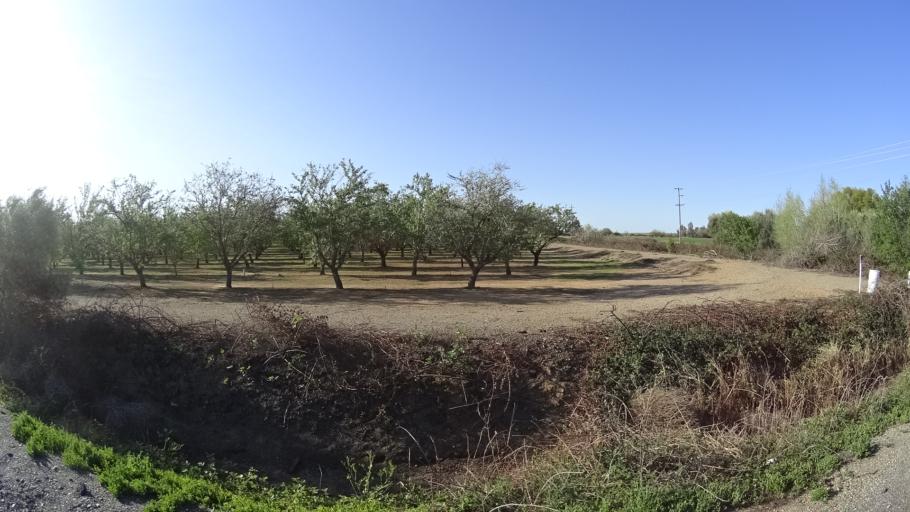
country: US
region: California
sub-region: Glenn County
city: Orland
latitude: 39.7976
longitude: -122.1406
